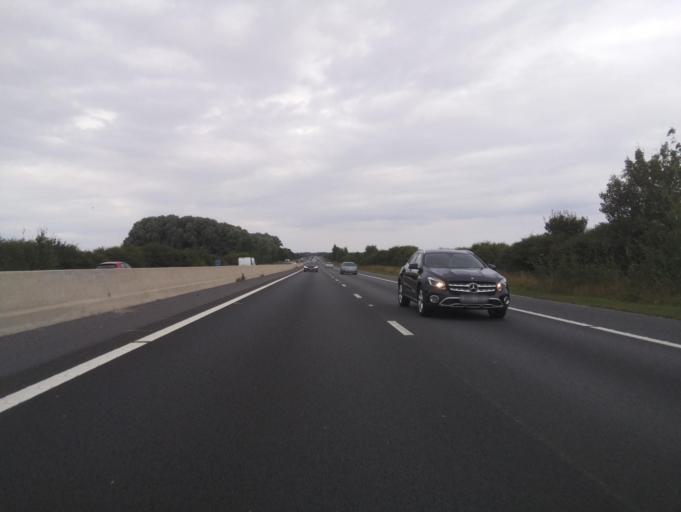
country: GB
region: England
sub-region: County Durham
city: Newton Aycliffe
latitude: 54.6215
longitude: -1.5288
